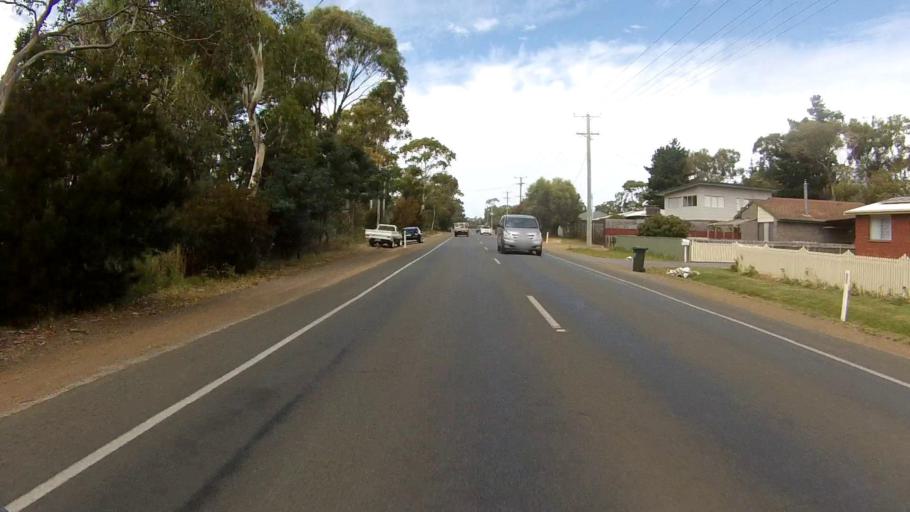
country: AU
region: Tasmania
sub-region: Clarence
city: Sandford
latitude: -42.9375
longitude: 147.4943
